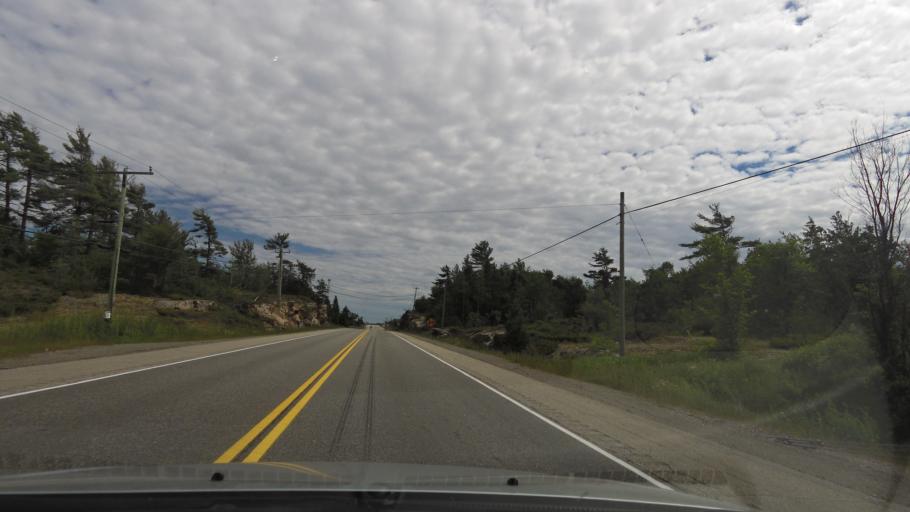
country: CA
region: Ontario
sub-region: Parry Sound District
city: Parry Sound
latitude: 45.8070
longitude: -80.5400
